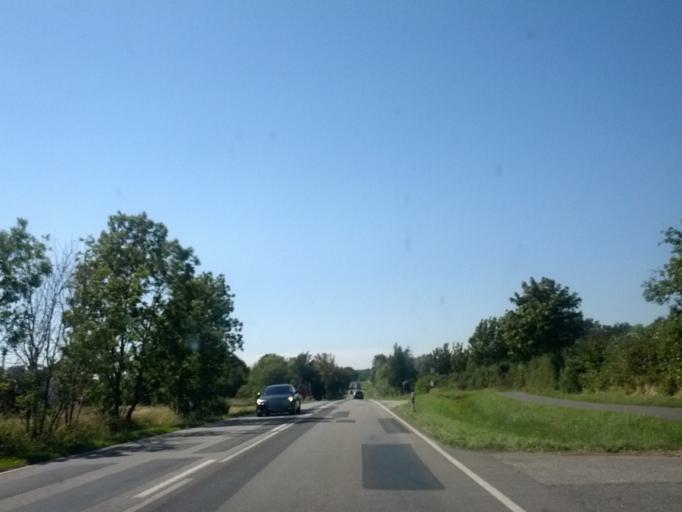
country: DE
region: Mecklenburg-Vorpommern
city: Sagard
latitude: 54.5047
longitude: 13.5306
